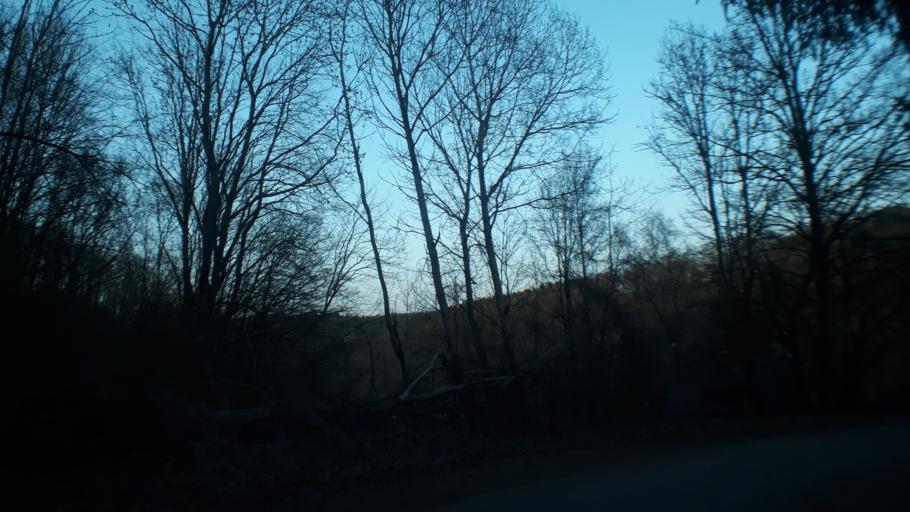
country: DE
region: Rheinland-Pfalz
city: Ohlenhard
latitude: 50.4873
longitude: 6.7406
